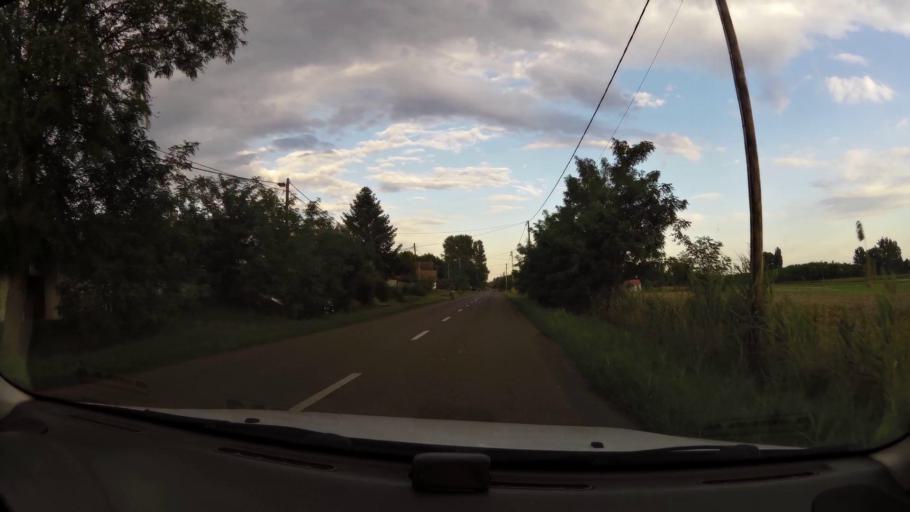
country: HU
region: Pest
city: Tapiobicske
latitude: 47.3722
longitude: 19.6754
